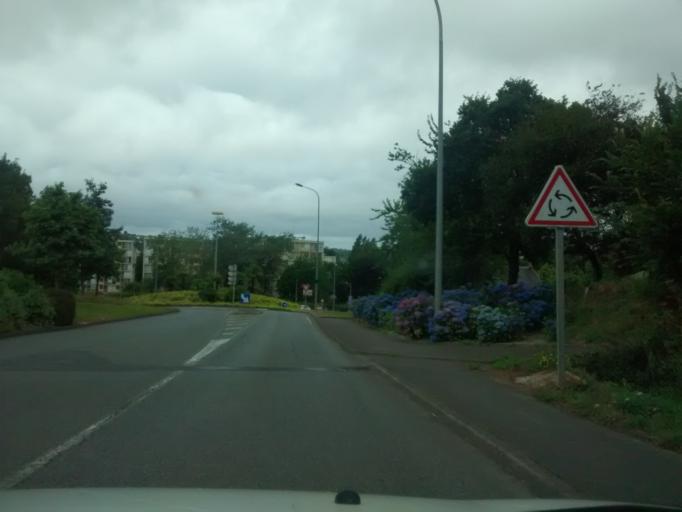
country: FR
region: Brittany
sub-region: Departement des Cotes-d'Armor
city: Lannion
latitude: 48.7264
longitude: -3.4444
